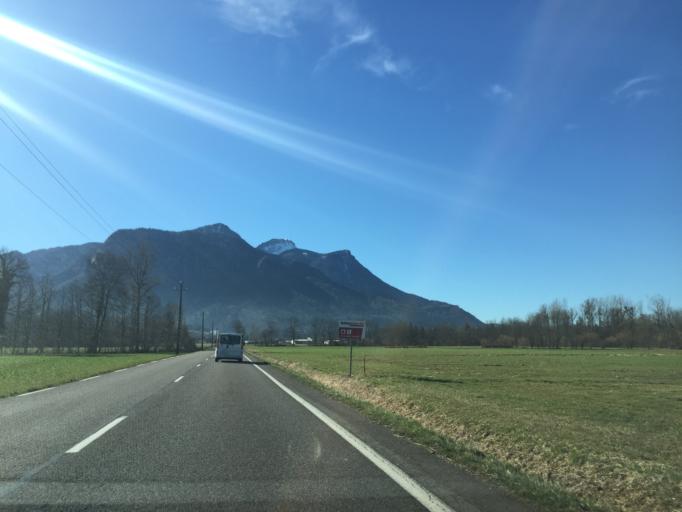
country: FR
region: Rhone-Alpes
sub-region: Departement de l'Isere
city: Saint-Laurent-du-Pont
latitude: 45.4077
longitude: 5.7468
